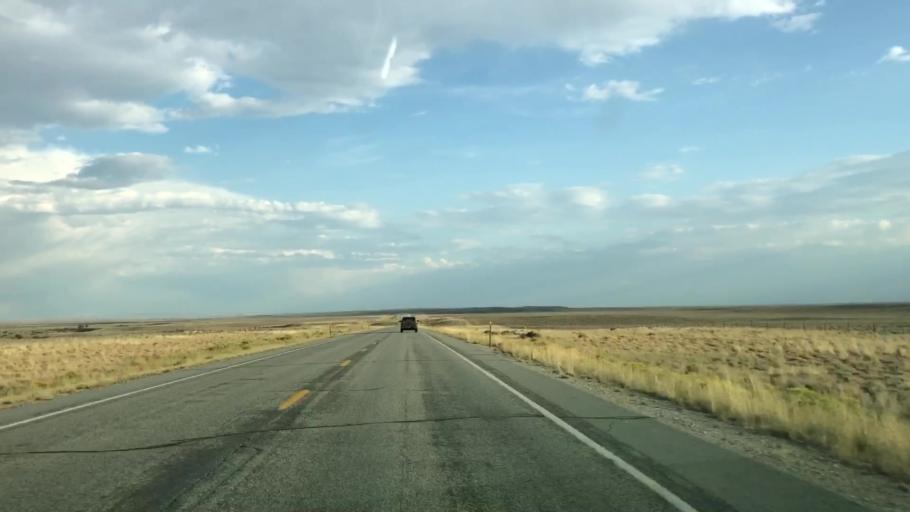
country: US
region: Wyoming
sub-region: Sublette County
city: Marbleton
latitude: 42.3332
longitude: -109.5177
